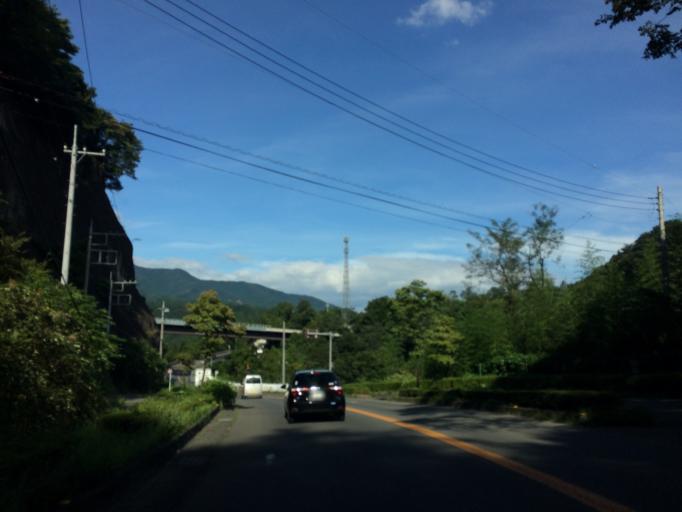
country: JP
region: Gunma
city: Shibukawa
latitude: 36.5430
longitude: 138.9425
